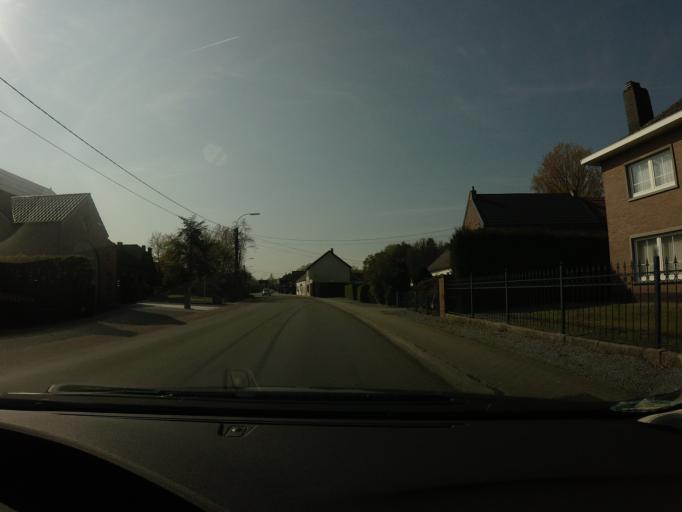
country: BE
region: Flanders
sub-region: Provincie Limburg
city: Maasmechelen
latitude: 50.9381
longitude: 5.6805
